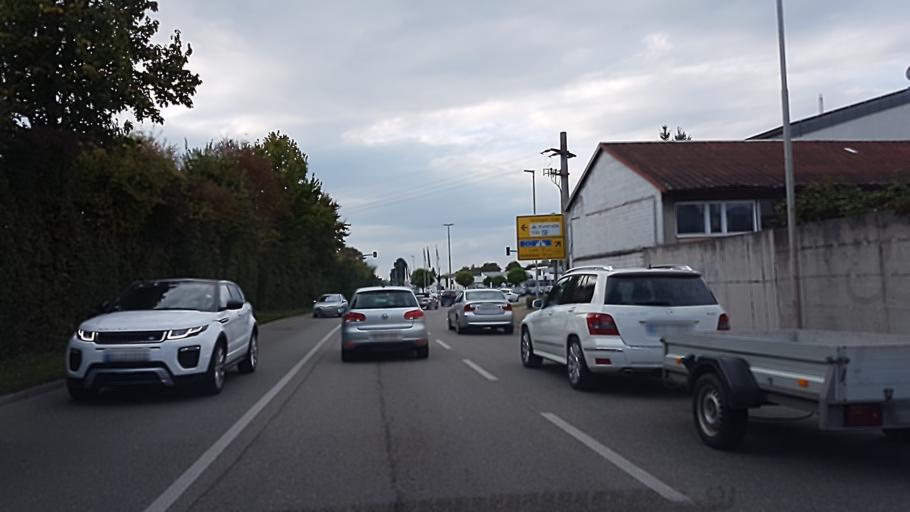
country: DE
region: Baden-Wuerttemberg
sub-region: Freiburg Region
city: Emmendingen
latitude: 48.1226
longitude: 7.8375
